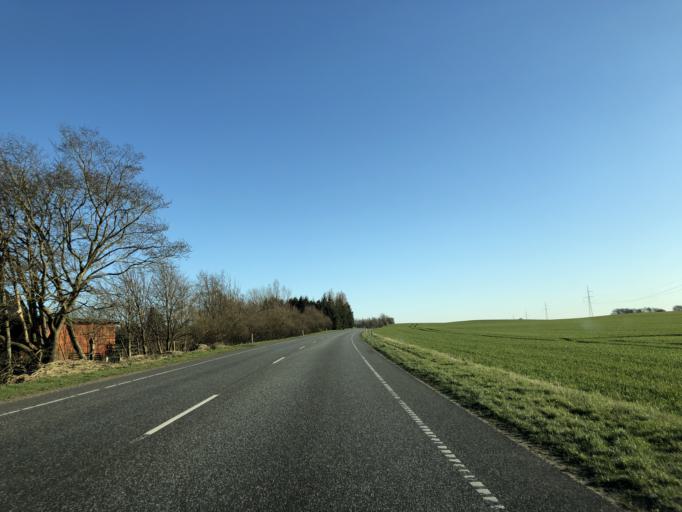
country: DK
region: North Denmark
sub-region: Vesthimmerland Kommune
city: Alestrup
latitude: 56.6865
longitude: 9.5335
